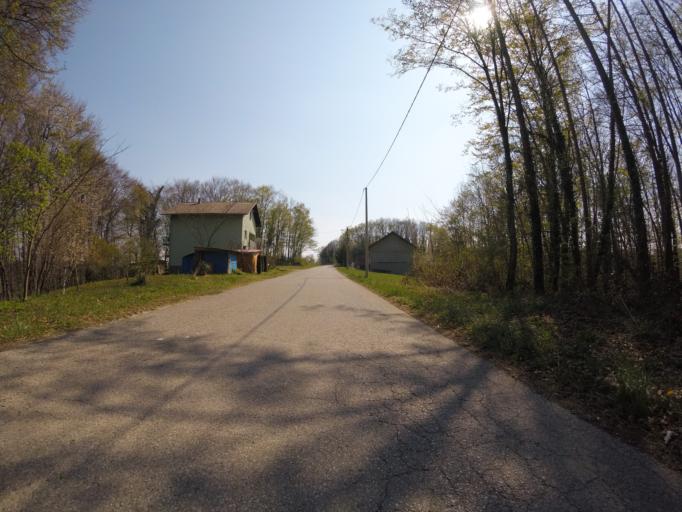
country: HR
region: Grad Zagreb
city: Strmec
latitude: 45.6187
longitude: 15.9496
